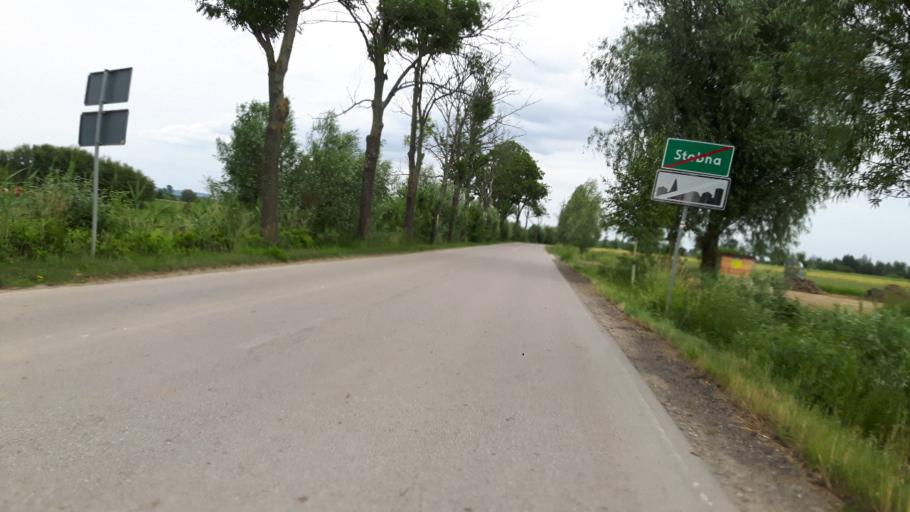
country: PL
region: Warmian-Masurian Voivodeship
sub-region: Powiat elblaski
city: Gronowo Elblaskie
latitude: 54.2004
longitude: 19.2848
